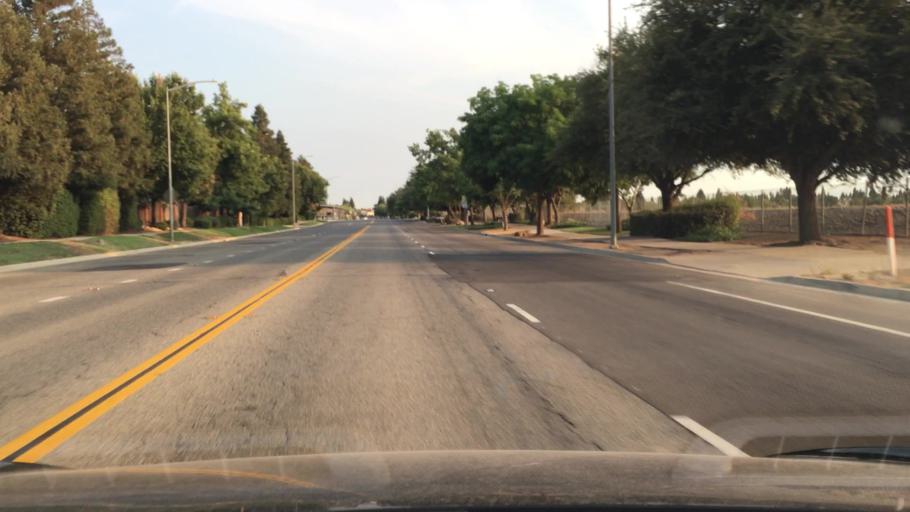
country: US
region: California
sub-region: Fresno County
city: Clovis
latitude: 36.8503
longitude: -119.6931
